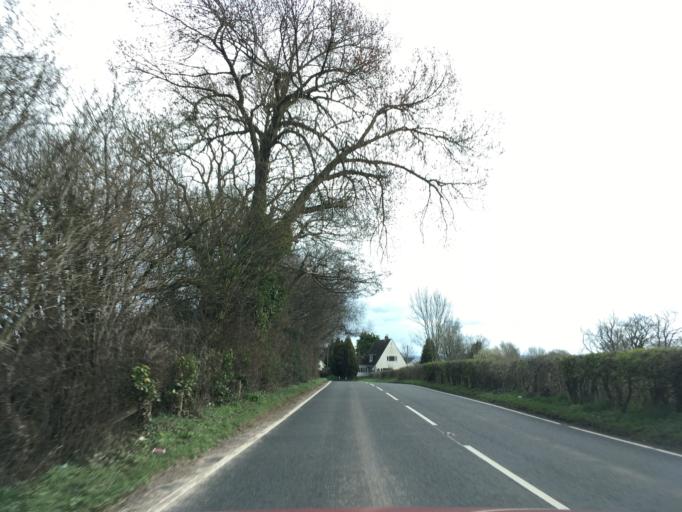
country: GB
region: England
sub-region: Gloucestershire
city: Cinderford
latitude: 51.8232
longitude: -2.4458
